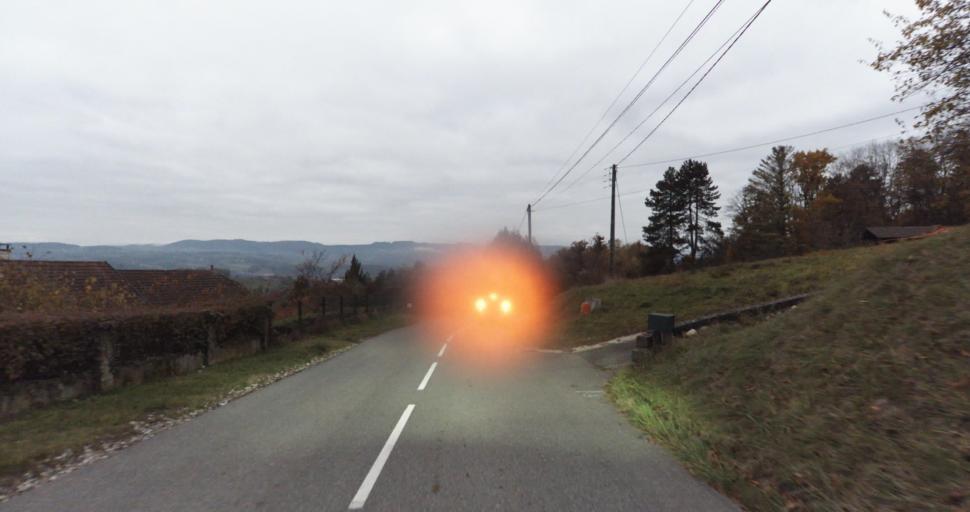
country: FR
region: Rhone-Alpes
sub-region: Departement de la Haute-Savoie
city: Alby-sur-Cheran
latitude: 45.8413
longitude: 6.0049
